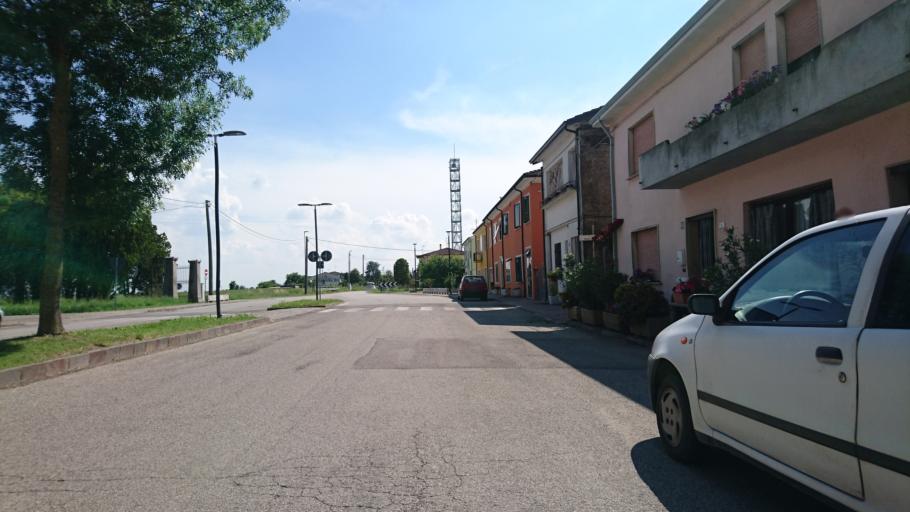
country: IT
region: Veneto
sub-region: Provincia di Rovigo
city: Castelmassa
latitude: 45.0587
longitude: 11.3295
